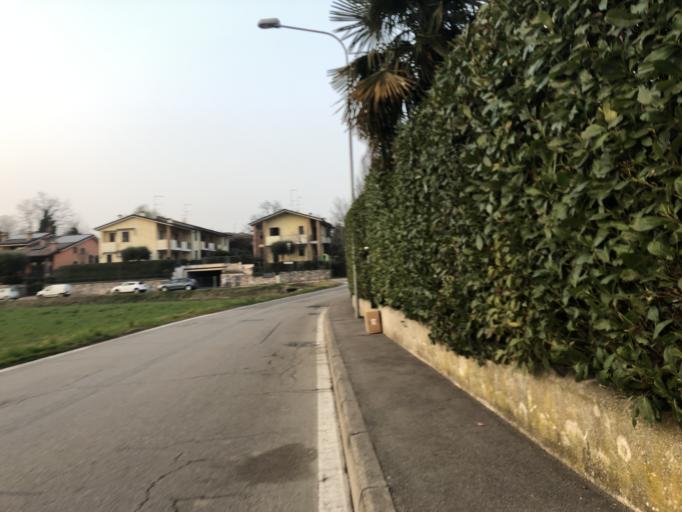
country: IT
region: Veneto
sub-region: Provincia di Verona
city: Sommacampagna
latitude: 45.4036
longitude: 10.8362
